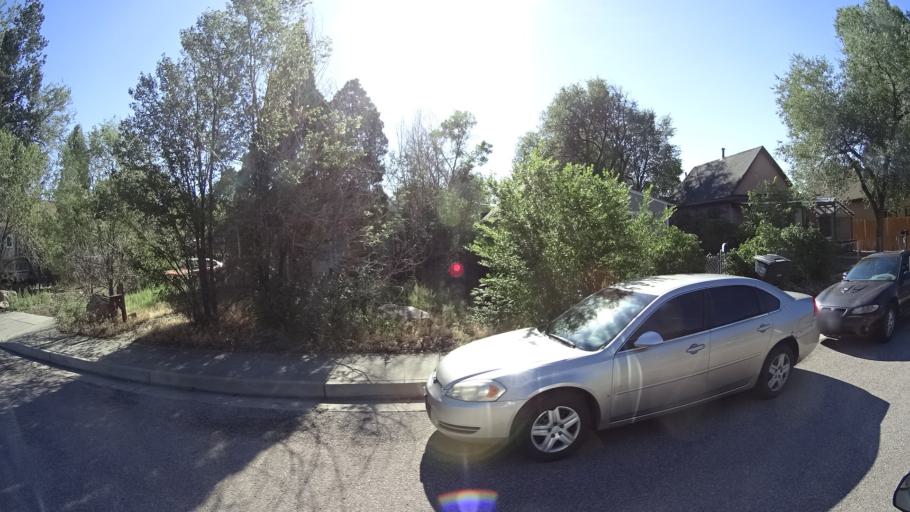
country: US
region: Colorado
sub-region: El Paso County
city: Colorado Springs
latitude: 38.8207
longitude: -104.8315
